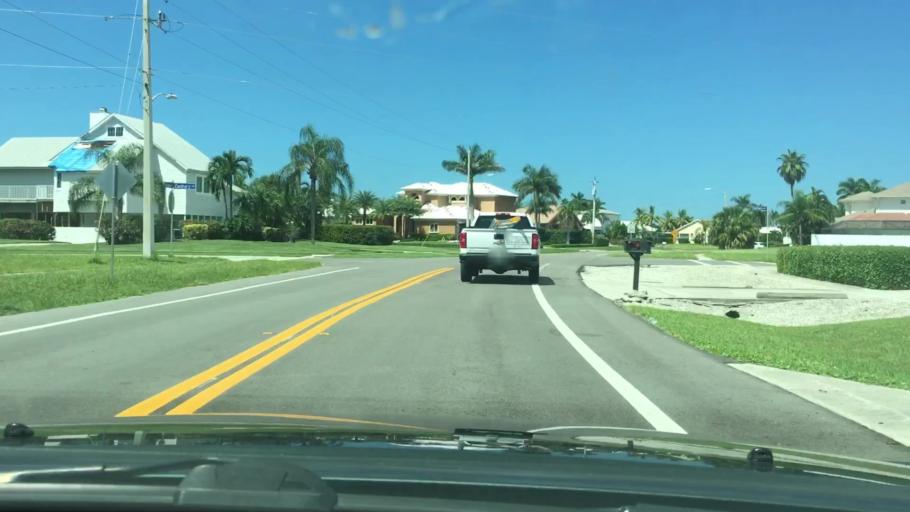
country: US
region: Florida
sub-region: Collier County
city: Marco
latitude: 25.9479
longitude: -81.7339
